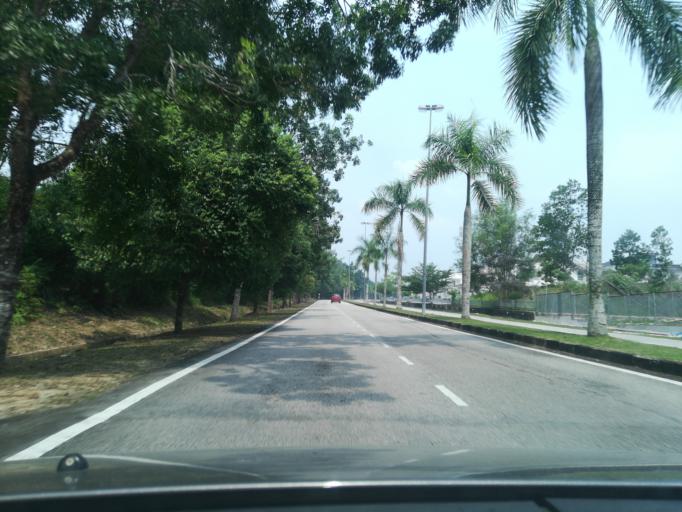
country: MY
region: Kedah
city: Kulim
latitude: 5.4000
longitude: 100.5767
